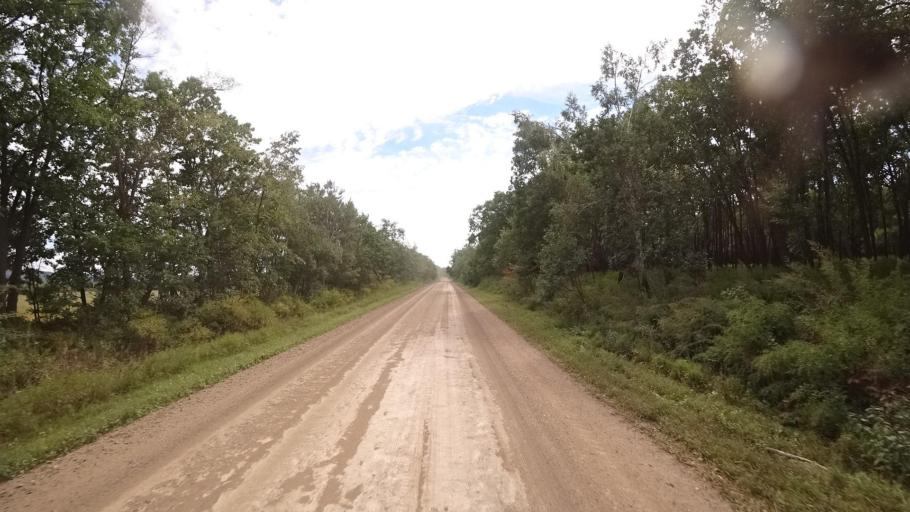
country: RU
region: Primorskiy
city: Yakovlevka
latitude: 44.5187
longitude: 133.5969
